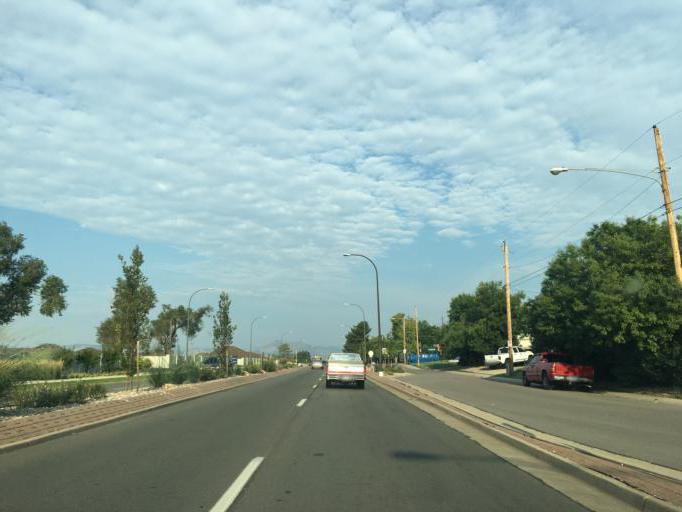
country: US
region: Colorado
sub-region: Jefferson County
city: Lakewood
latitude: 39.6822
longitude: -105.0729
